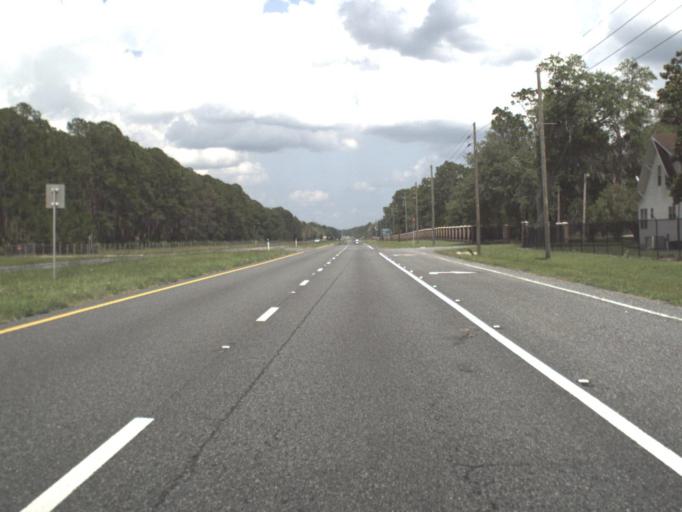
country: US
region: Florida
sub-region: Bradford County
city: Starke
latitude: 29.9818
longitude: -81.9906
